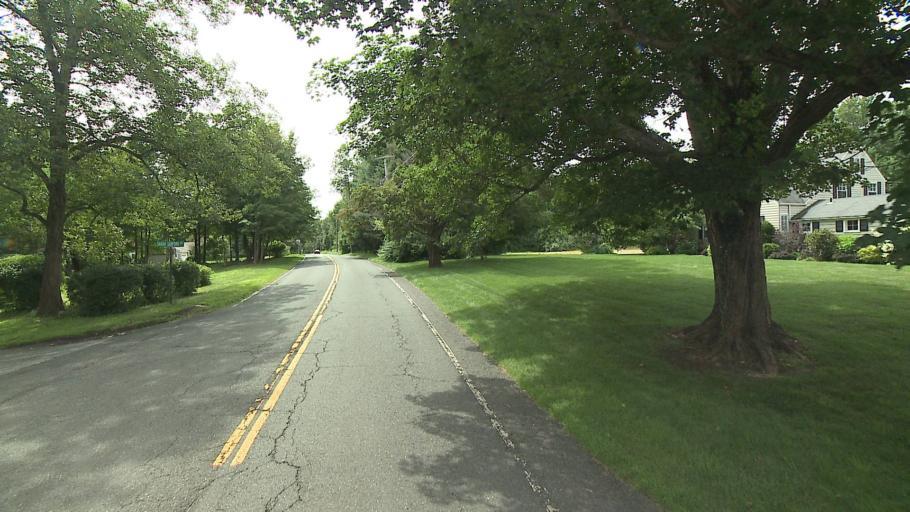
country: US
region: Connecticut
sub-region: Litchfield County
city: New Milford
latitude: 41.5269
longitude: -73.3653
